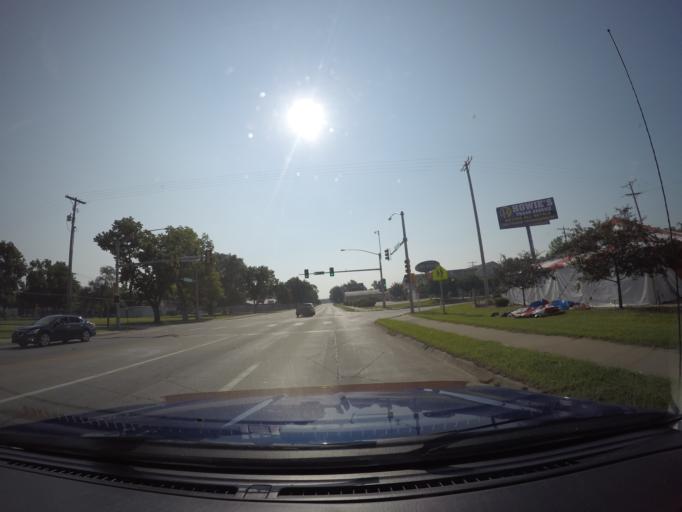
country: US
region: Kansas
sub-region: Riley County
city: Manhattan
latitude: 39.1742
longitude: -96.5724
